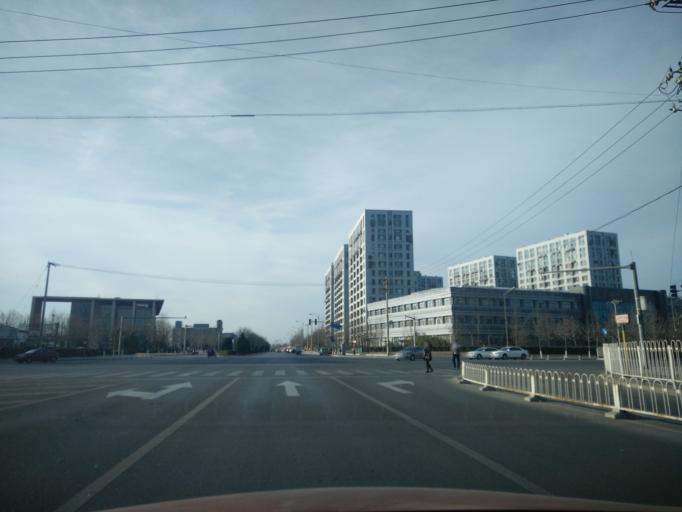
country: CN
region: Beijing
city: Jiugong
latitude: 39.7694
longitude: 116.4965
